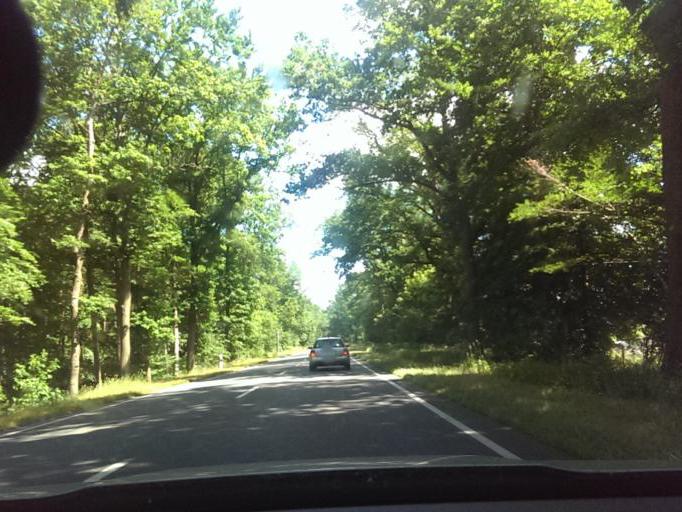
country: DE
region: Lower Saxony
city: Ahausen
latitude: 53.0143
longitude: 9.2760
